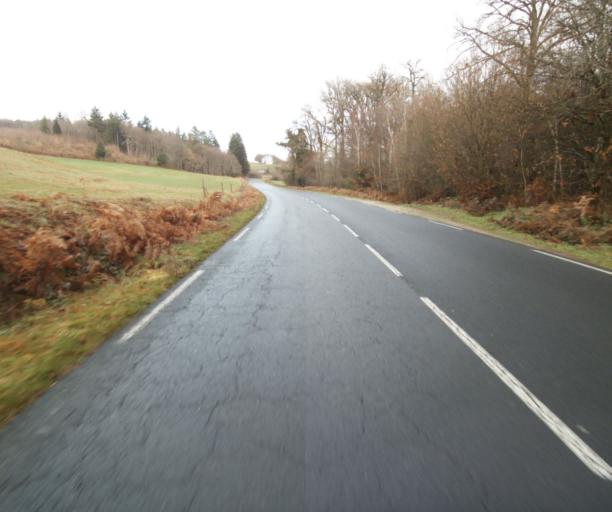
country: FR
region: Limousin
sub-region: Departement de la Correze
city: Saint-Mexant
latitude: 45.2731
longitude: 1.6454
